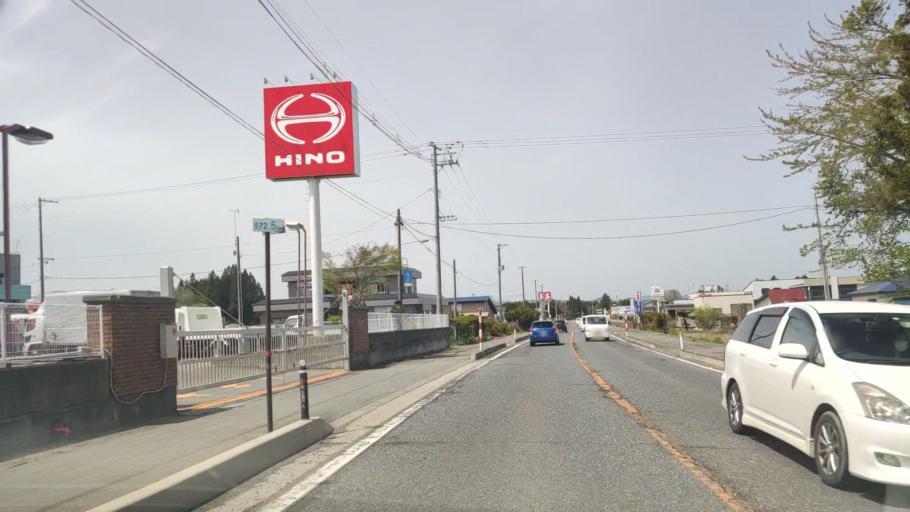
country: JP
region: Aomori
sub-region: Misawa Shi
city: Inuotose
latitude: 40.6744
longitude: 141.1774
